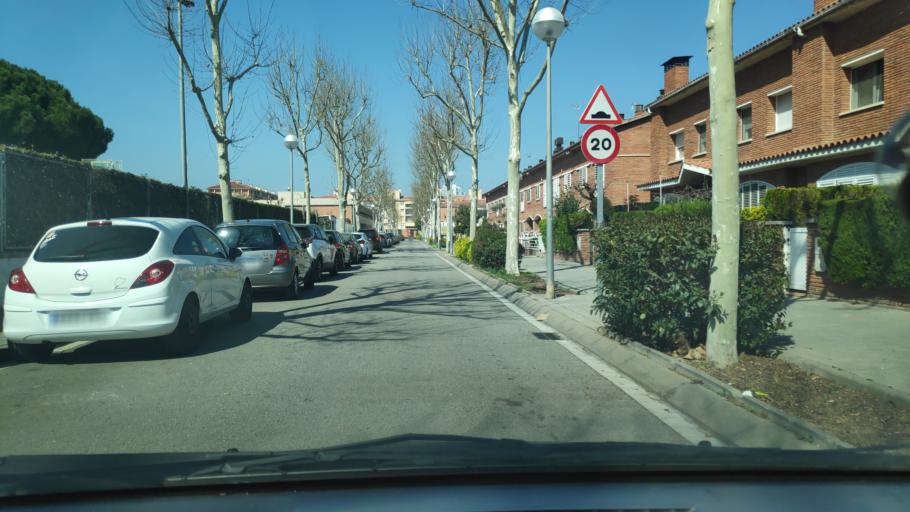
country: ES
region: Catalonia
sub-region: Provincia de Barcelona
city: Mollet del Valles
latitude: 41.5433
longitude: 2.2044
